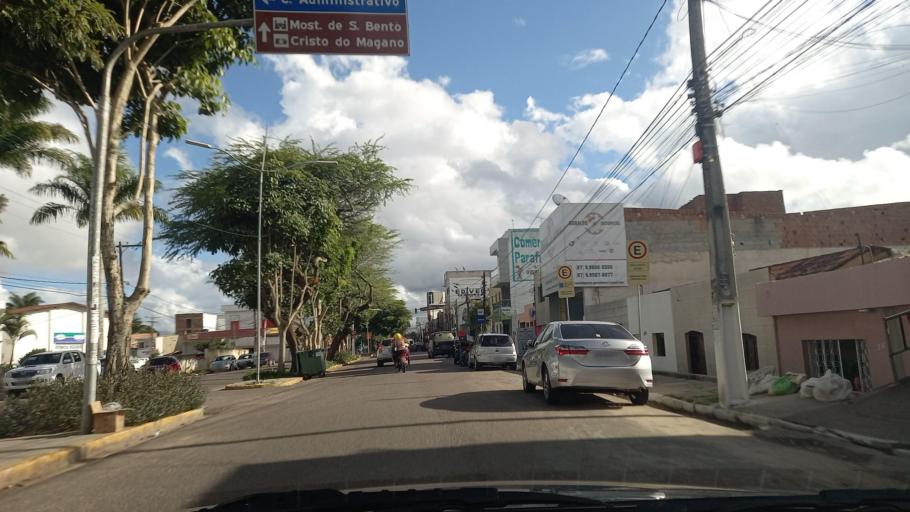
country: BR
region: Pernambuco
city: Garanhuns
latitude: -8.8833
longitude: -36.4880
